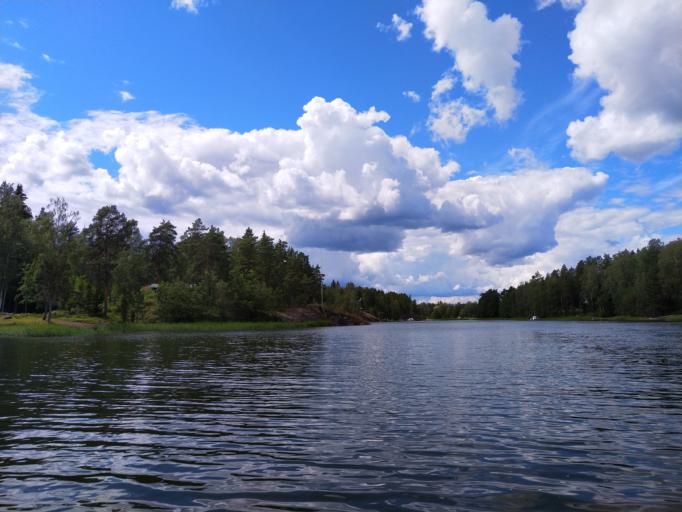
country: FI
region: Uusimaa
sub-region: Raaseporin
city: Karis
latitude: 59.9701
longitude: 23.7151
